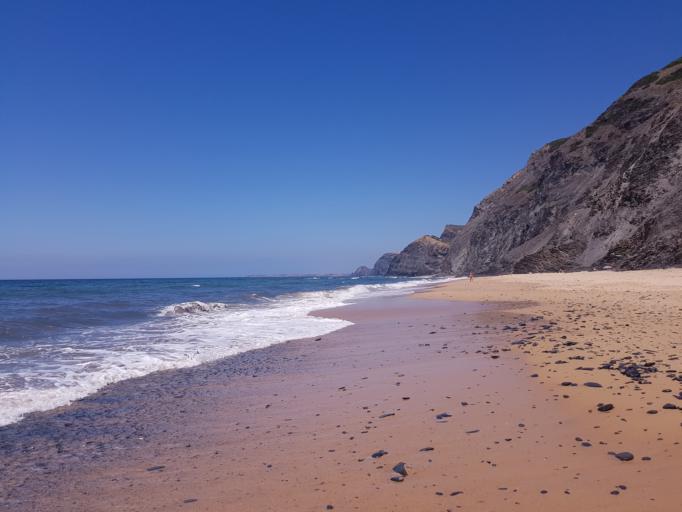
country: PT
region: Faro
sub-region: Vila do Bispo
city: Vila do Bispo
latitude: 37.1139
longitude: -8.9340
